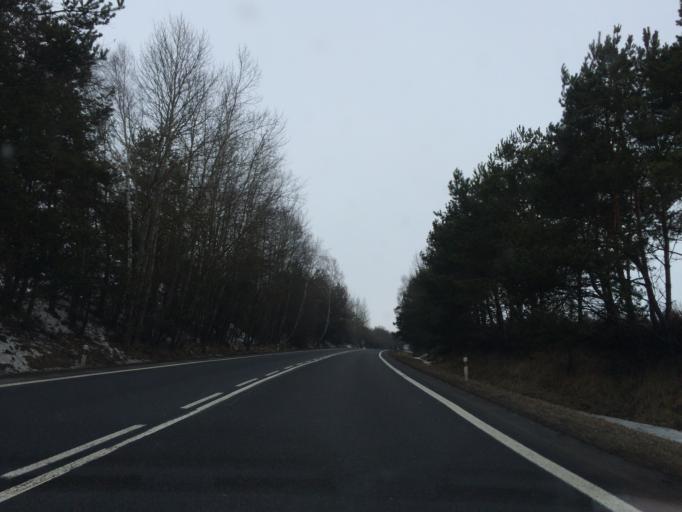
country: CZ
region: Jihocesky
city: Mirotice
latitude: 49.4169
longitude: 14.0370
